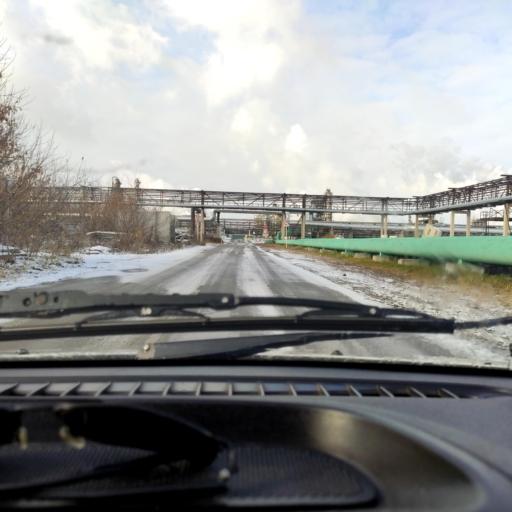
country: RU
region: Samara
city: Tol'yatti
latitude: 53.5363
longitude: 49.4702
